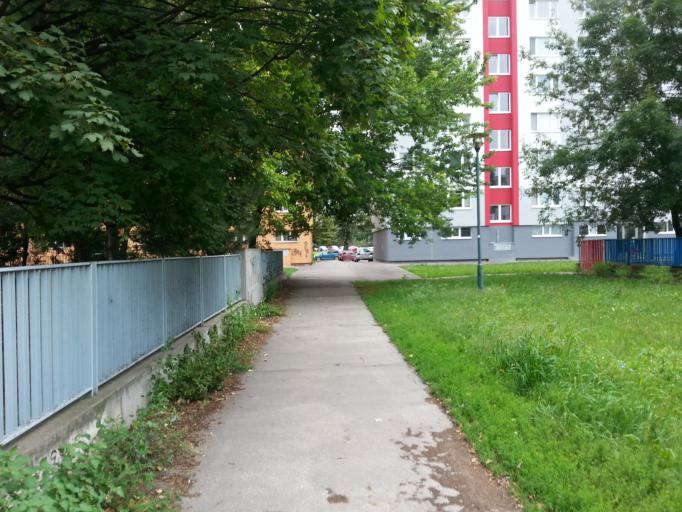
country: SK
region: Bratislavsky
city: Bratislava
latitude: 48.1280
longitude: 17.1025
